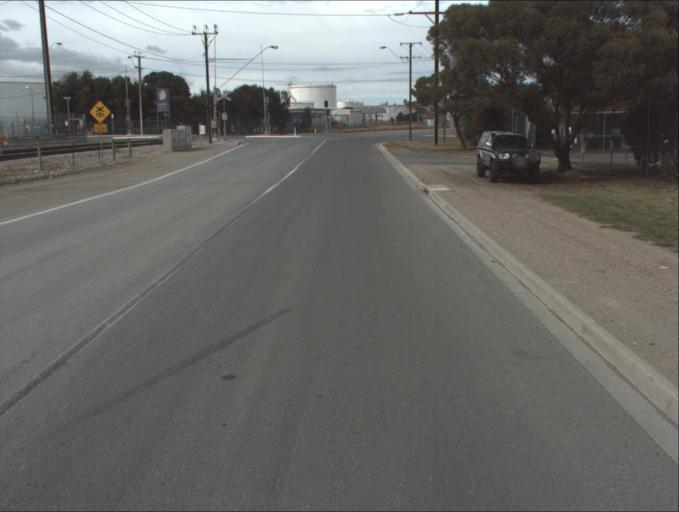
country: AU
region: South Australia
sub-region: Port Adelaide Enfield
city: Birkenhead
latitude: -34.8211
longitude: 138.5068
